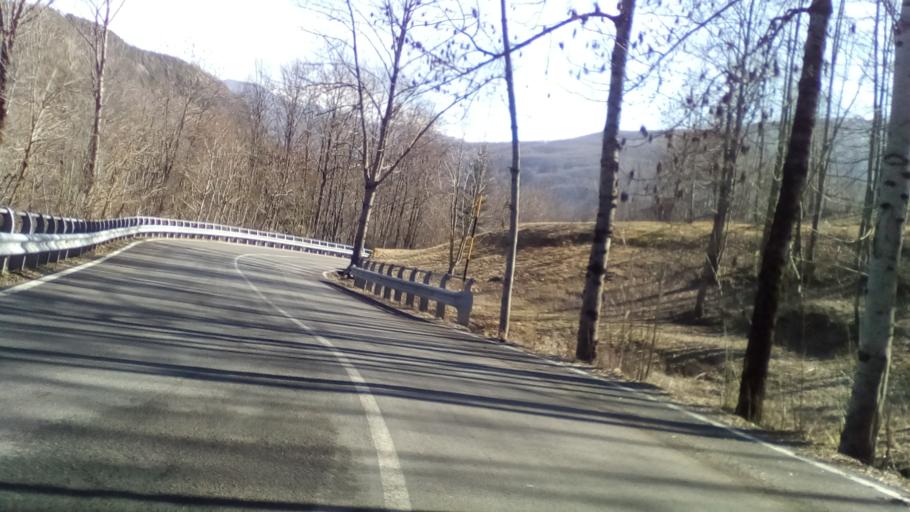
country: IT
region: Emilia-Romagna
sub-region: Provincia di Modena
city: Pievepelago
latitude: 44.1901
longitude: 10.5571
